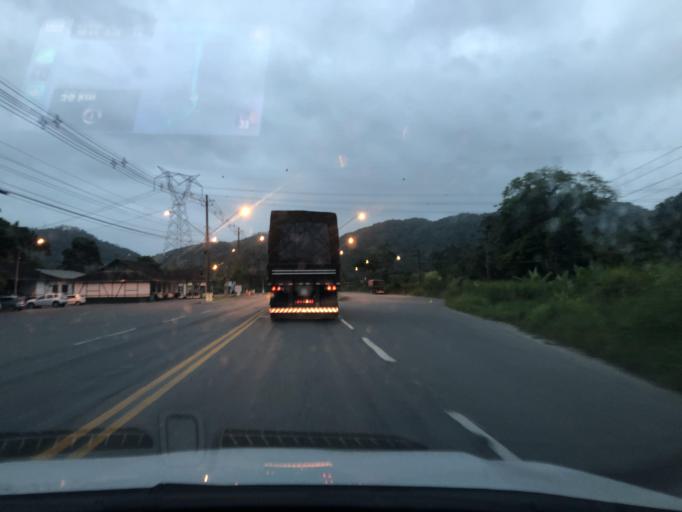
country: BR
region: Santa Catarina
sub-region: Pomerode
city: Pomerode
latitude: -26.7639
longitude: -49.0780
